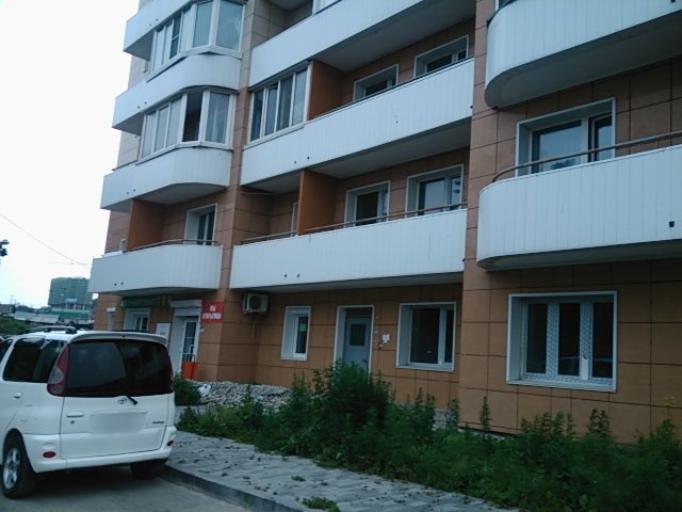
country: RU
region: Primorskiy
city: Vladivostok
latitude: 43.0874
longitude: 131.8559
